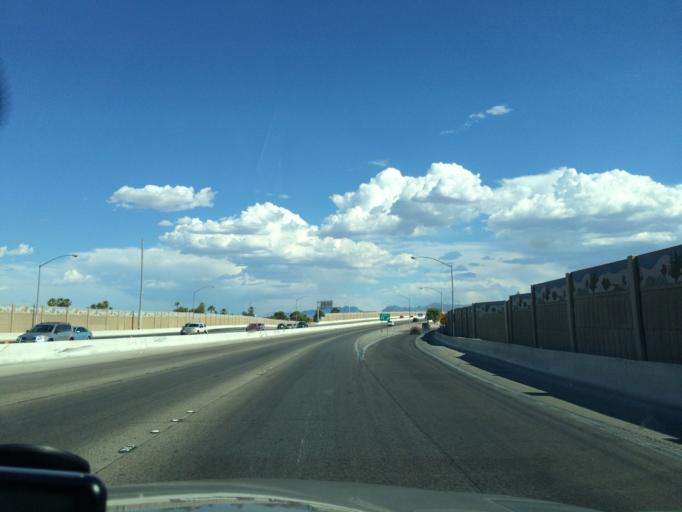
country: US
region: Nevada
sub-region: Clark County
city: Winchester
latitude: 36.1635
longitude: -115.0934
